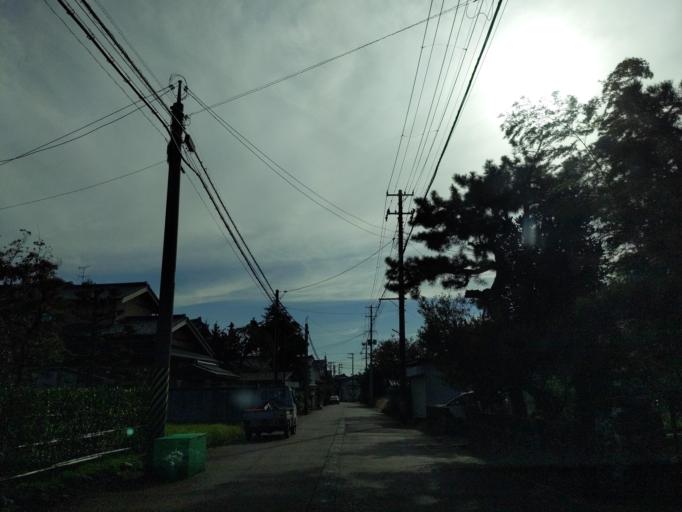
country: JP
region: Niigata
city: Sanjo
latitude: 37.6193
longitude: 138.9441
